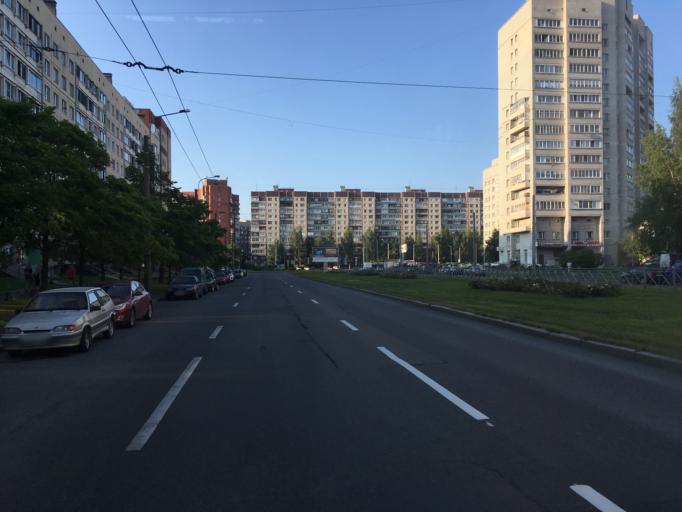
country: RU
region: St.-Petersburg
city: Komendantsky aerodrom
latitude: 60.0115
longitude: 30.2629
